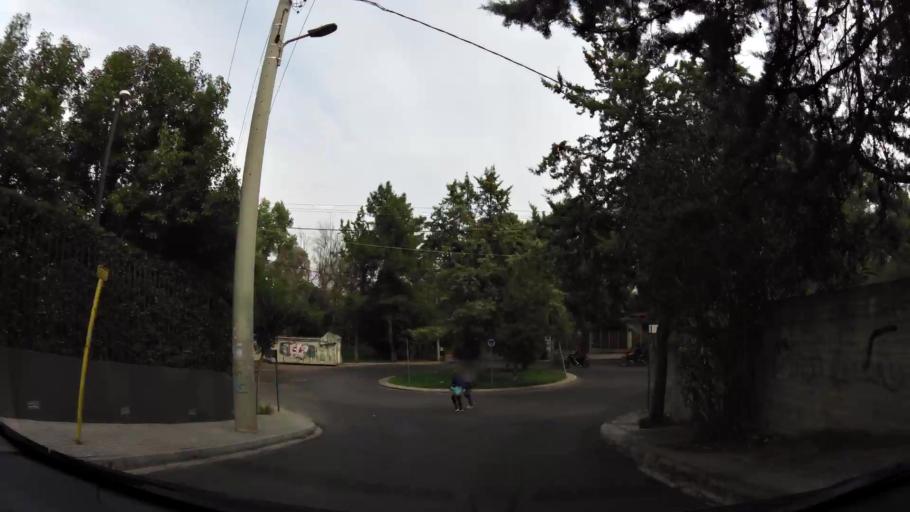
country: GR
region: Attica
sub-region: Nomarchia Athinas
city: Filothei
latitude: 38.0311
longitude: 23.7742
